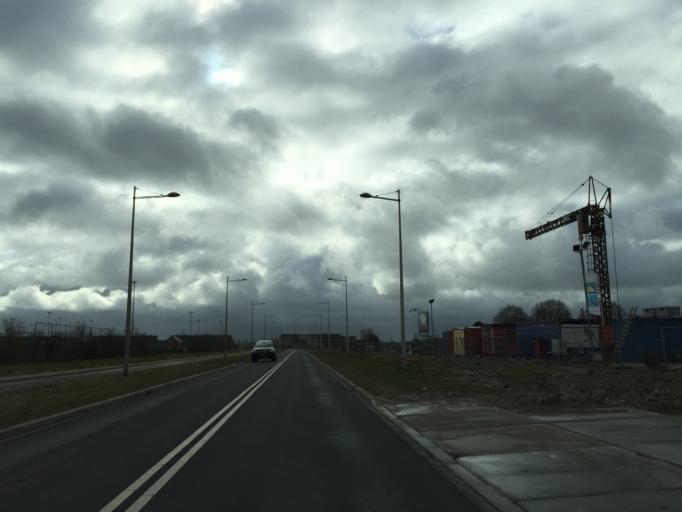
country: NL
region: South Holland
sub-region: Gemeente Lansingerland
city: Berkel en Rodenrijs
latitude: 52.0038
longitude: 4.4749
